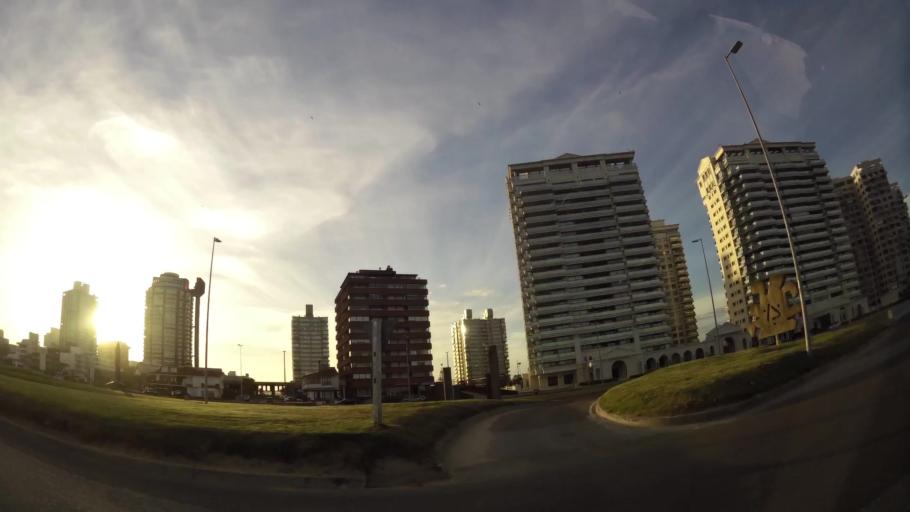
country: UY
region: Maldonado
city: Punta del Este
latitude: -34.9570
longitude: -54.9369
